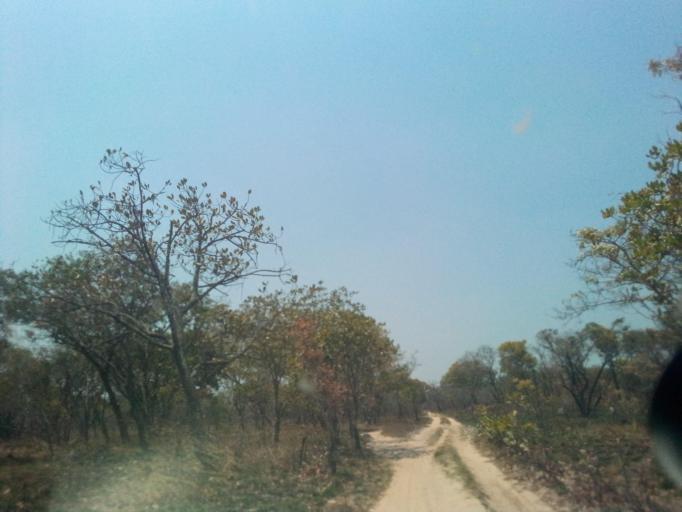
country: ZM
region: Copperbelt
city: Kataba
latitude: -12.2420
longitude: 30.4007
